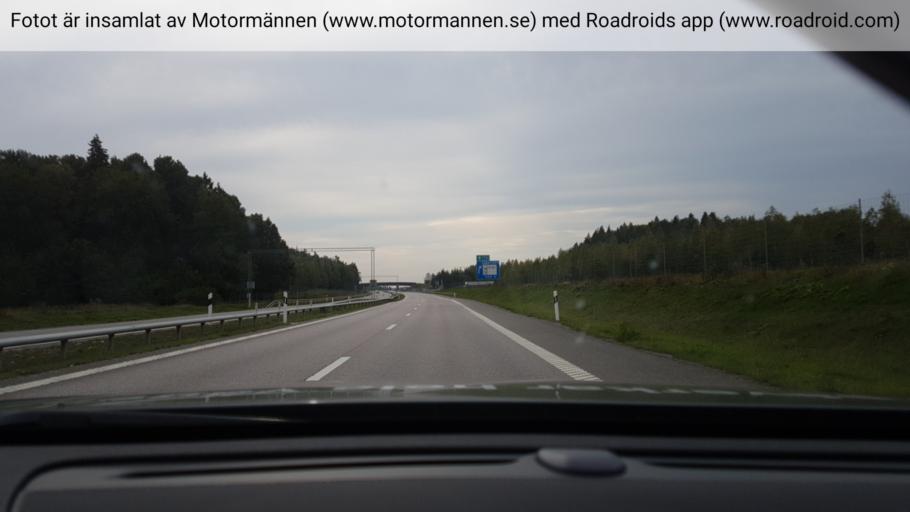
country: SE
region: Stockholm
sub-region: Nynashamns Kommun
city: Osmo
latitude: 58.9694
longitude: 17.9088
